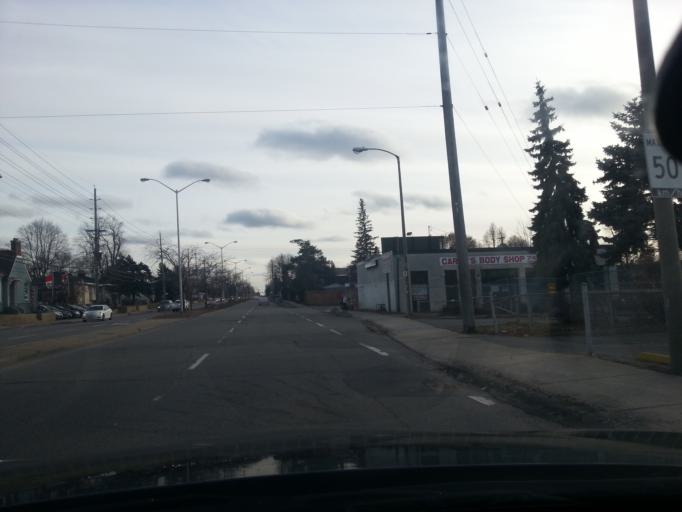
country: CA
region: Ontario
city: Ottawa
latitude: 45.4407
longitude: -75.6467
